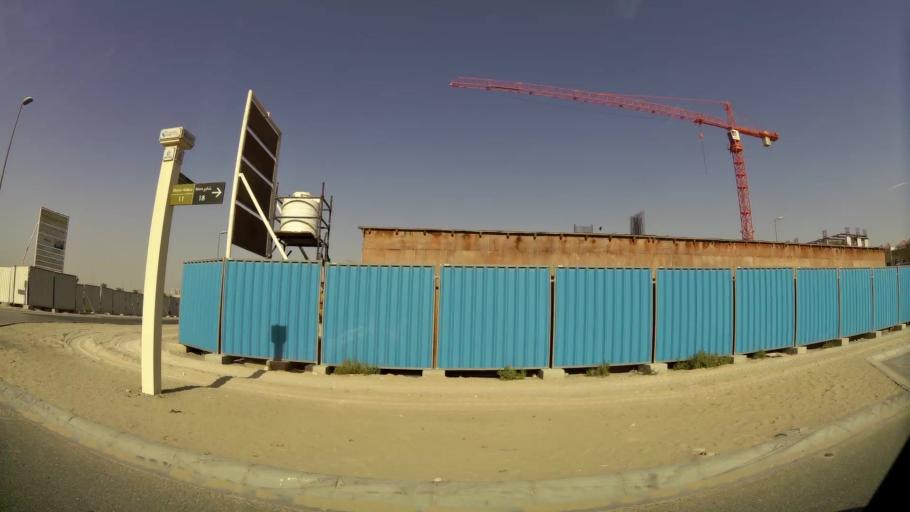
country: AE
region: Dubai
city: Dubai
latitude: 25.0667
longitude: 55.2116
